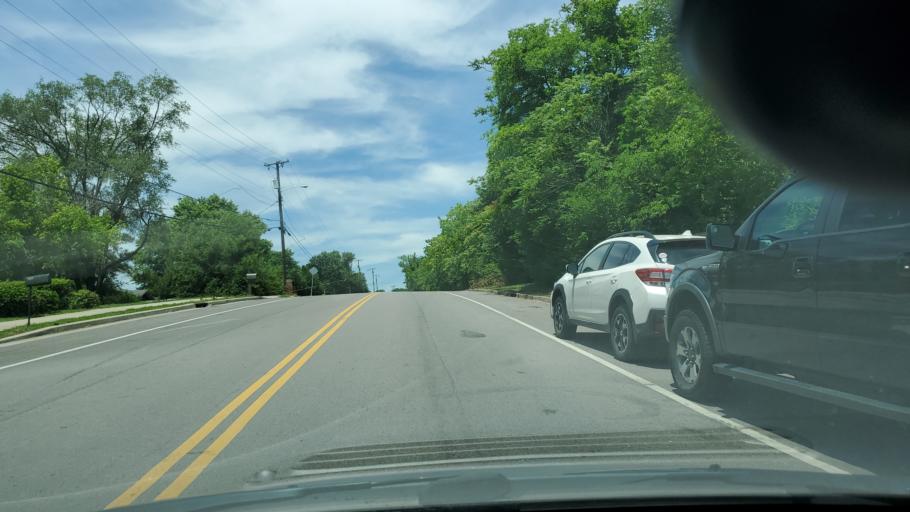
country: US
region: Tennessee
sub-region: Davidson County
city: Nashville
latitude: 36.2140
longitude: -86.7533
